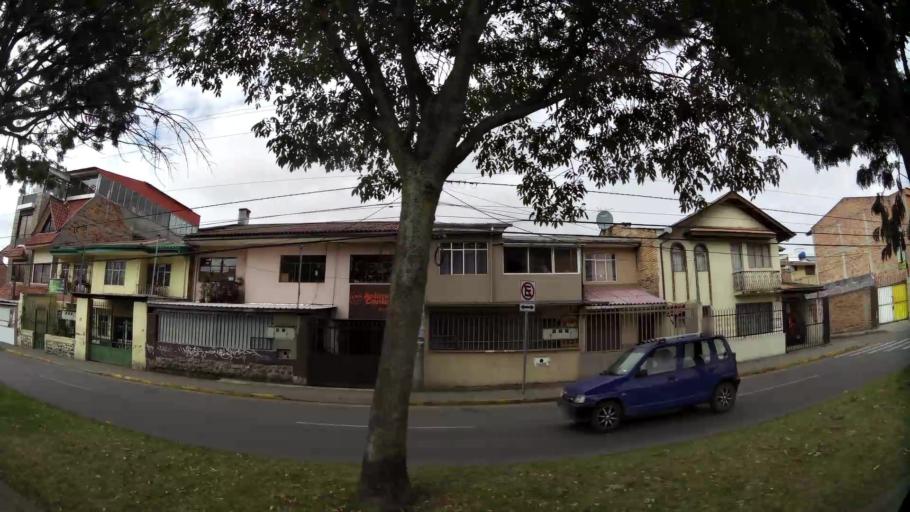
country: EC
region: Azuay
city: Cuenca
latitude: -2.8906
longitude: -78.9767
